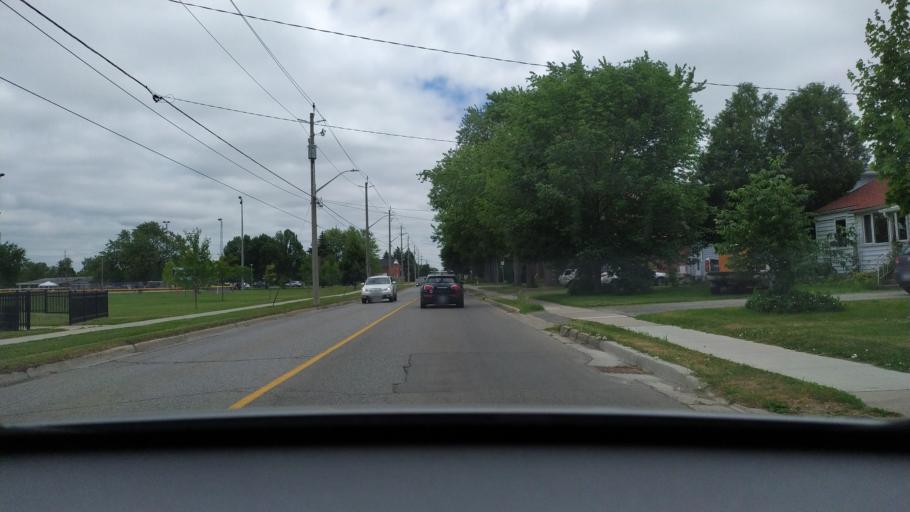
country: CA
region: Ontario
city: Stratford
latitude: 43.3577
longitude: -80.9750
